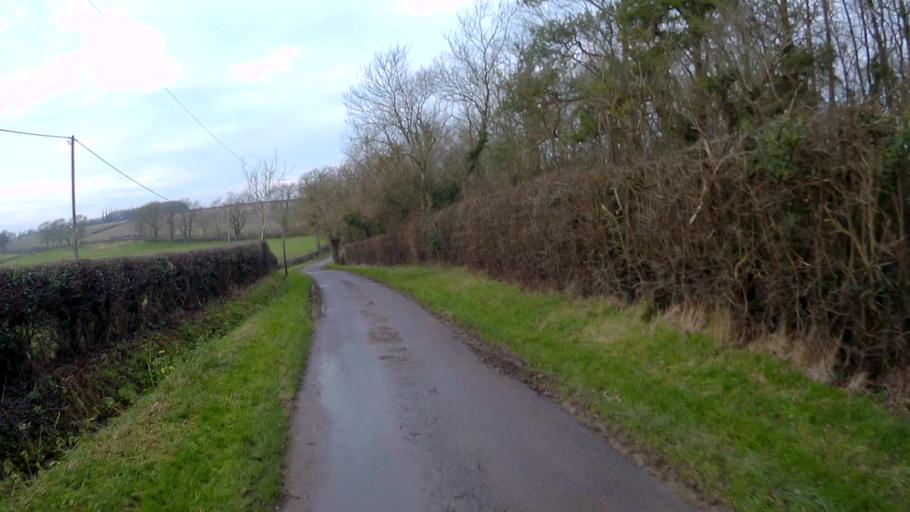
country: GB
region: England
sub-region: Lincolnshire
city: Bourne
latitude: 52.8260
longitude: -0.4603
